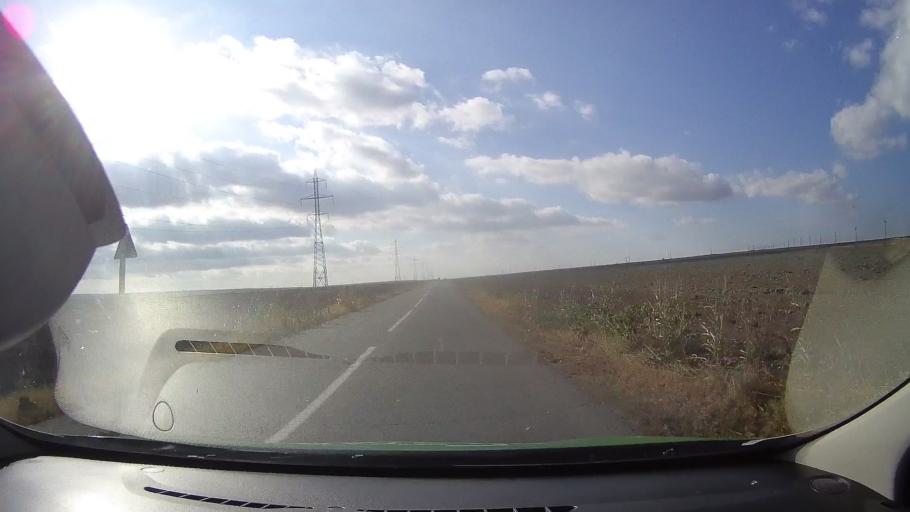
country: RO
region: Constanta
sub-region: Comuna Sacele
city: Sacele
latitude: 44.5104
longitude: 28.6776
